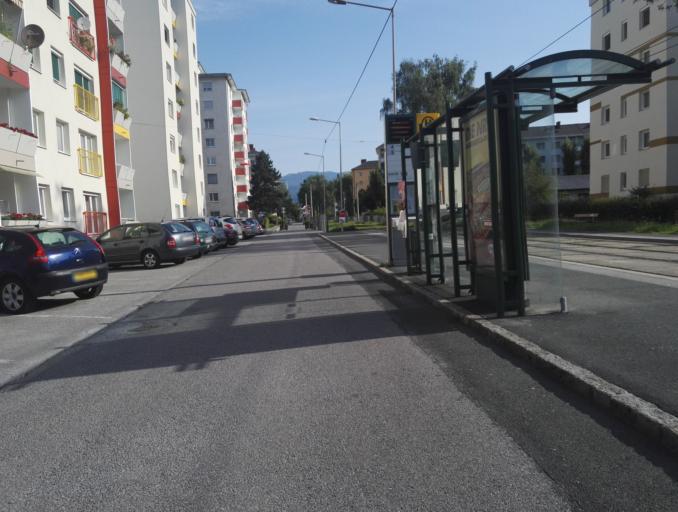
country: AT
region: Styria
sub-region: Graz Stadt
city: Goesting
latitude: 47.0990
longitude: 15.4210
